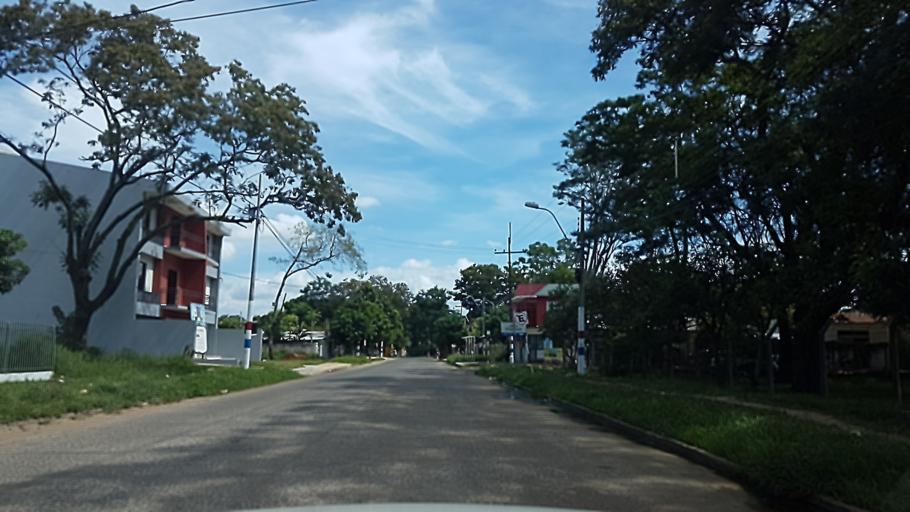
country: PY
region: Central
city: Colonia Mariano Roque Alonso
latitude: -25.1957
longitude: -57.5349
